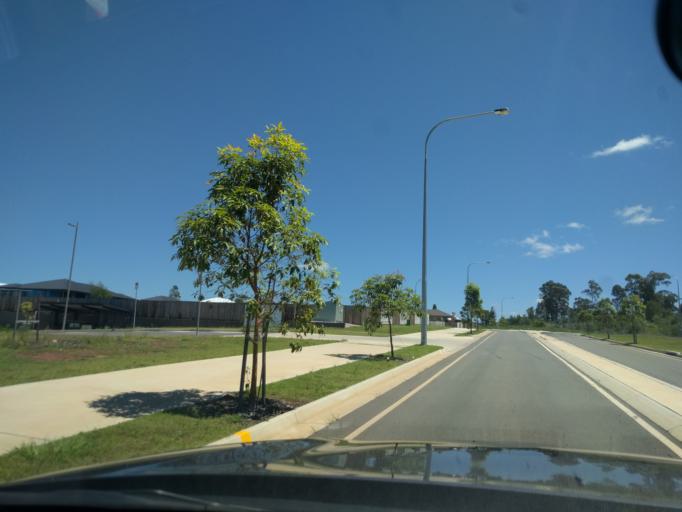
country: AU
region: Queensland
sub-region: Logan
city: Cedar Vale
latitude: -27.9895
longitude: 153.0127
